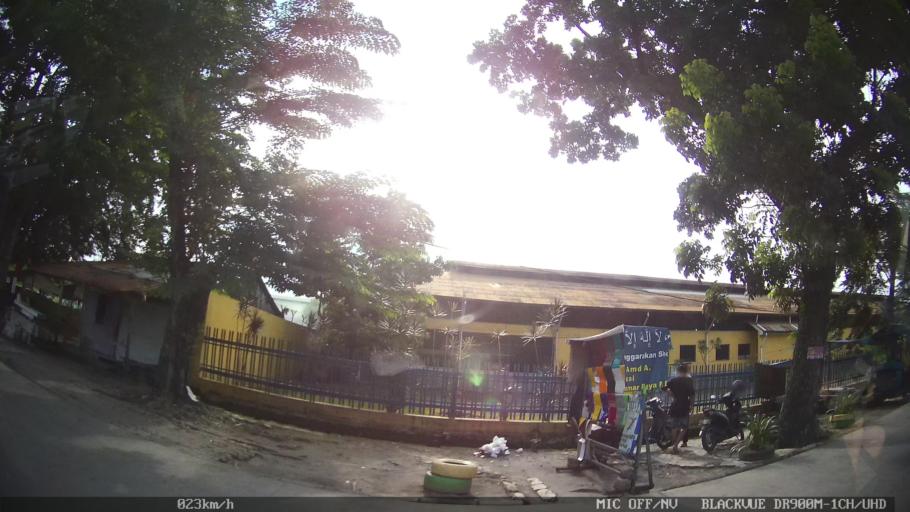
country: ID
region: North Sumatra
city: Medan
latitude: 3.6247
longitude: 98.6809
